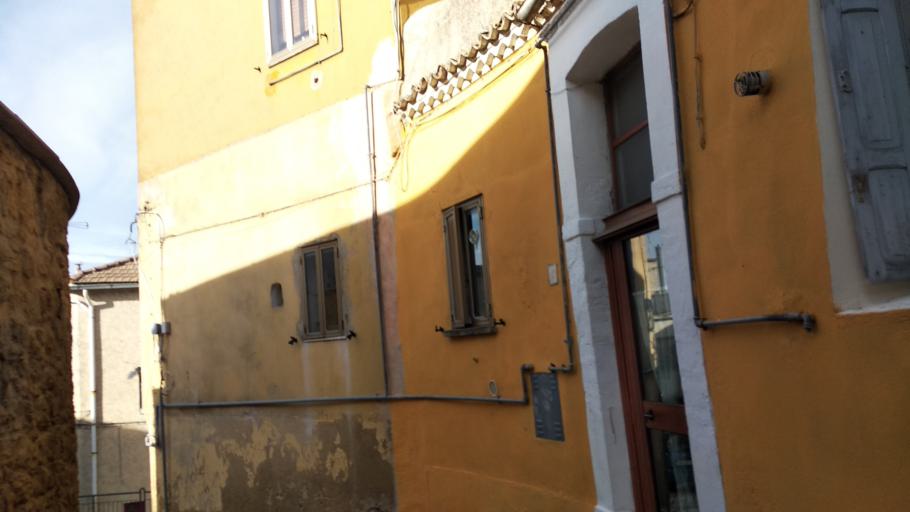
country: IT
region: Basilicate
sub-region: Provincia di Matera
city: Tricarico
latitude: 40.6224
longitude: 16.1450
